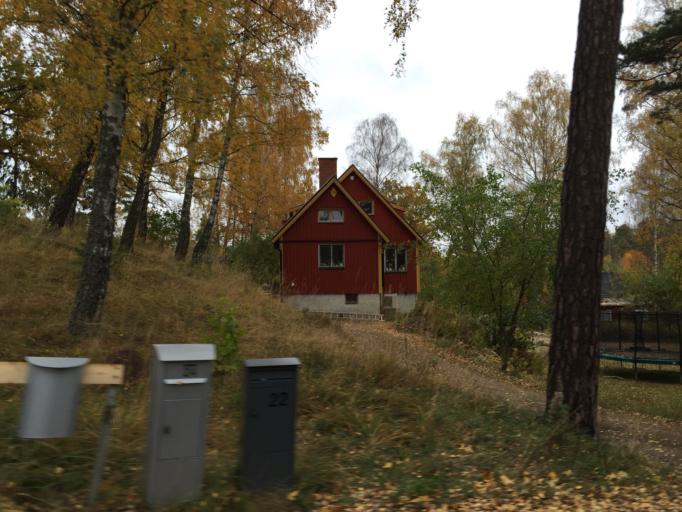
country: SE
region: Stockholm
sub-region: Salems Kommun
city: Ronninge
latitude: 59.1915
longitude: 17.7300
